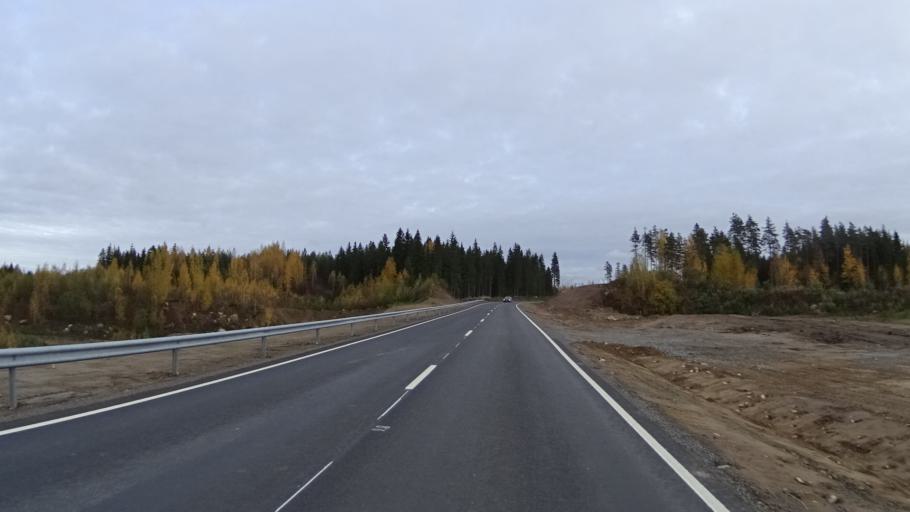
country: FI
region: South Karelia
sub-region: Lappeenranta
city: Taipalsaari
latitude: 61.0203
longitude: 28.0021
